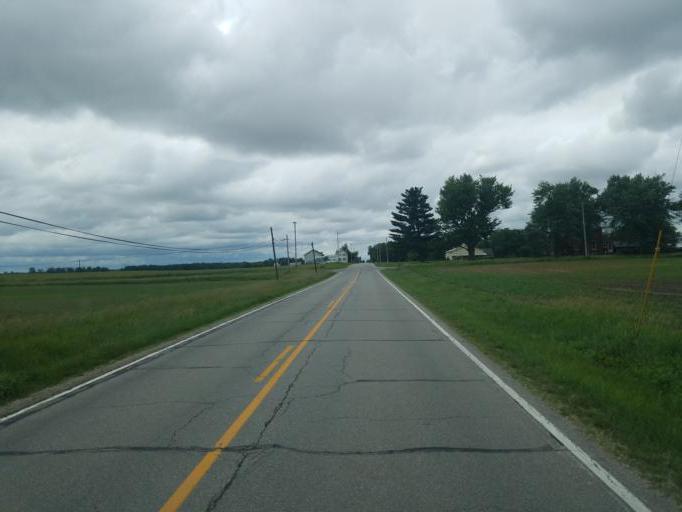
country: US
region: Ohio
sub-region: Crawford County
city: Bucyrus
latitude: 40.7624
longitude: -82.9539
